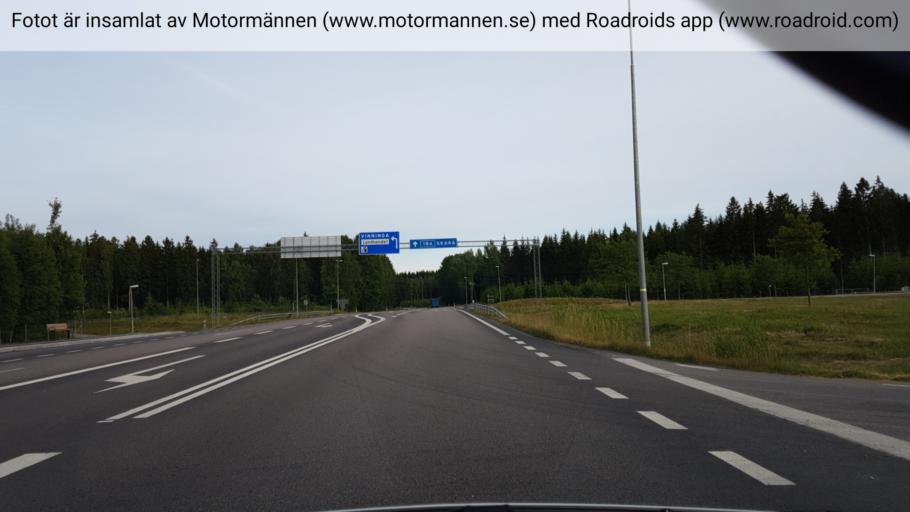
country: SE
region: Vaestra Goetaland
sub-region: Lidkopings Kommun
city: Vinninga
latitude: 58.4487
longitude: 13.2436
